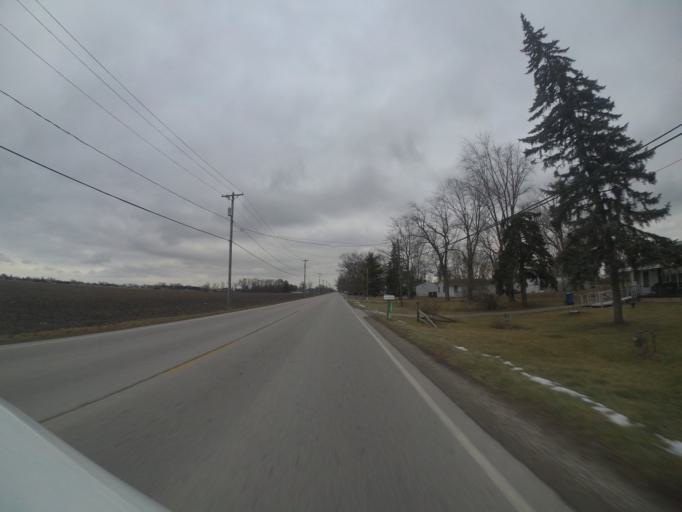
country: US
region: Ohio
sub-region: Wood County
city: Walbridge
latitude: 41.5823
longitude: -83.5124
